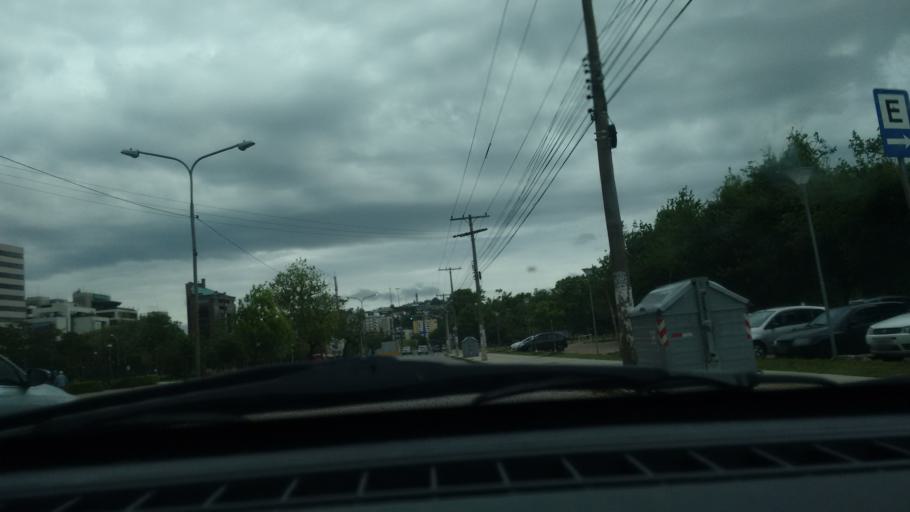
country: BR
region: Rio Grande do Sul
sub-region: Porto Alegre
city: Porto Alegre
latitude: -30.0555
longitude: -51.2304
